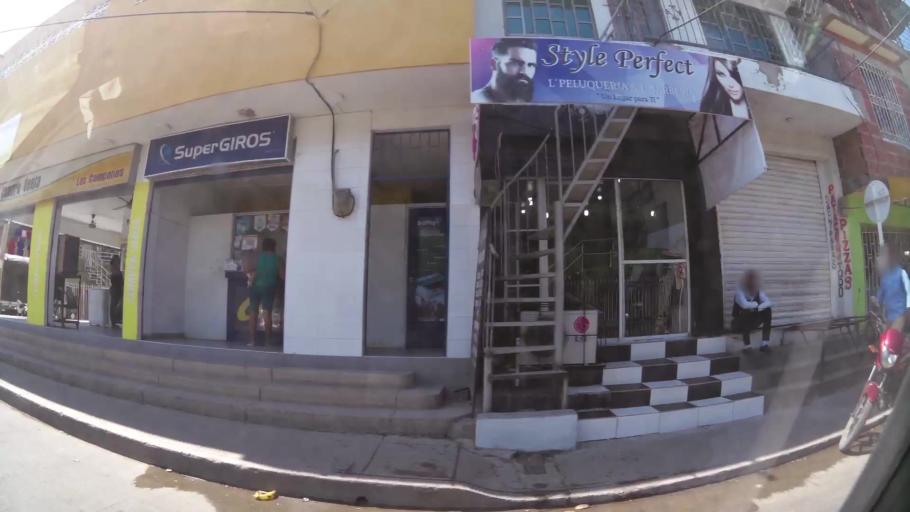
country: CO
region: Bolivar
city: Cartagena
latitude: 10.3859
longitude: -75.4579
